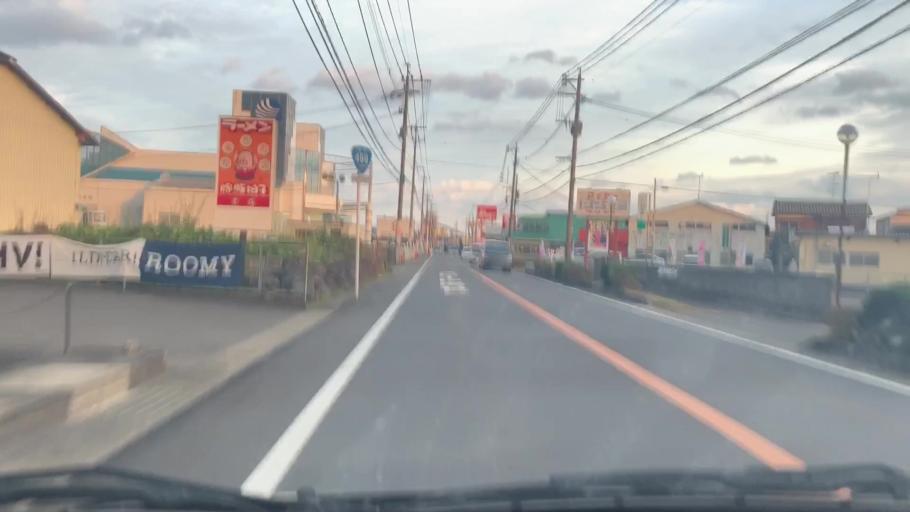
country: JP
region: Saga Prefecture
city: Kashima
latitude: 33.1222
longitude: 130.0863
